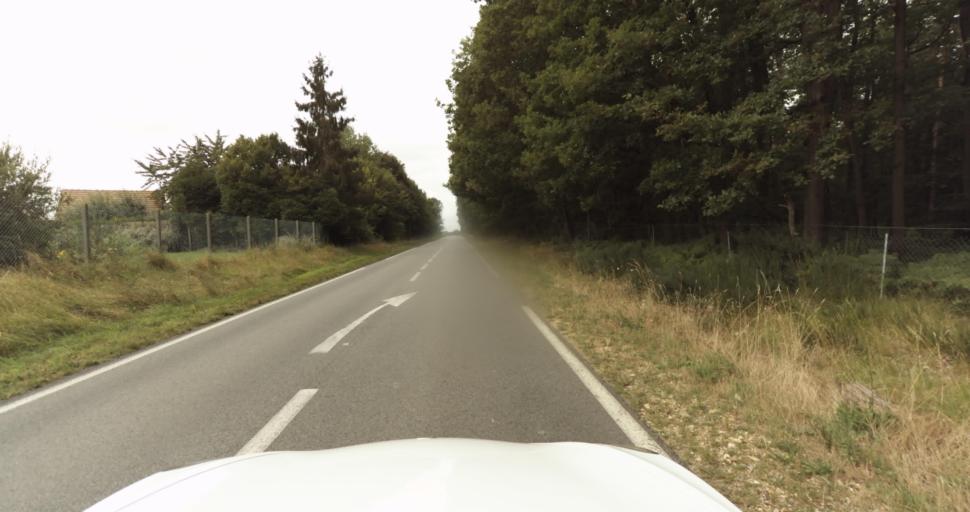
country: FR
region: Haute-Normandie
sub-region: Departement de l'Eure
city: Saint-Sebastien-de-Morsent
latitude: 49.0008
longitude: 1.0410
